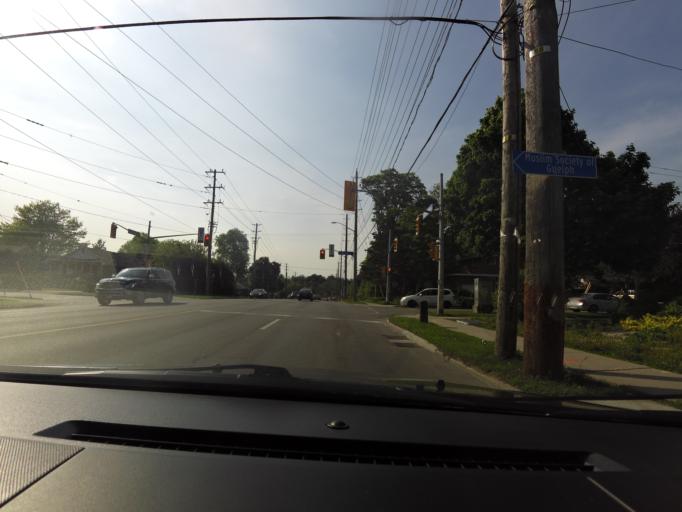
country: CA
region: Ontario
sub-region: Wellington County
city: Guelph
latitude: 43.5319
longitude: -80.2506
